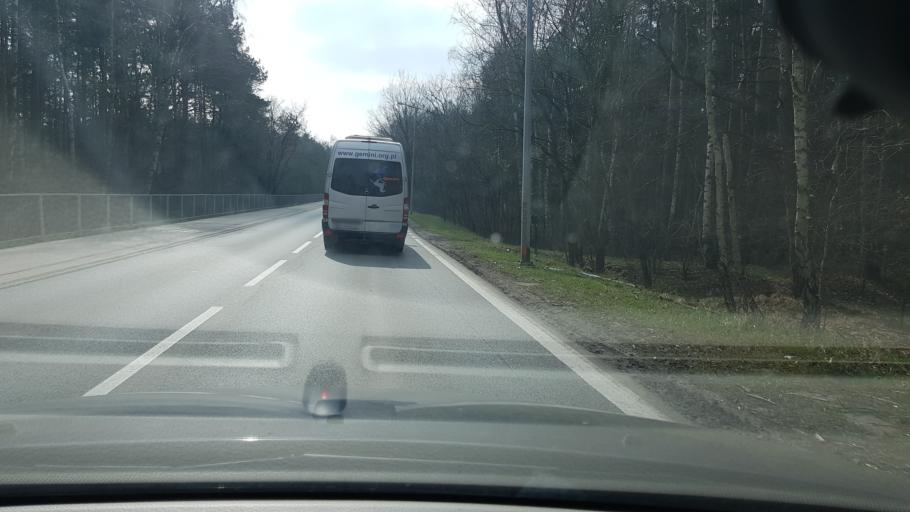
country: PL
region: Masovian Voivodeship
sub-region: Warszawa
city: Wesola
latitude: 52.2296
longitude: 21.2241
